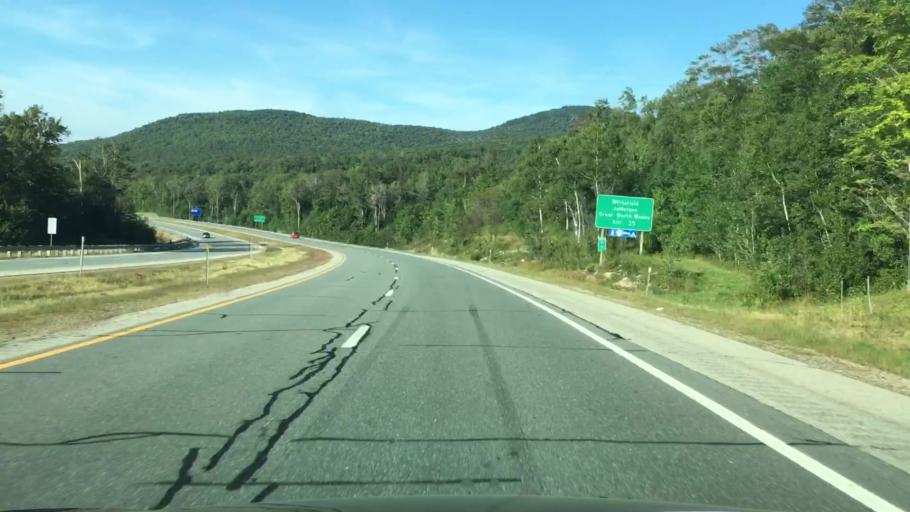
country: US
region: New Hampshire
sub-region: Grafton County
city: Deerfield
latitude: 44.1866
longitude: -71.6829
